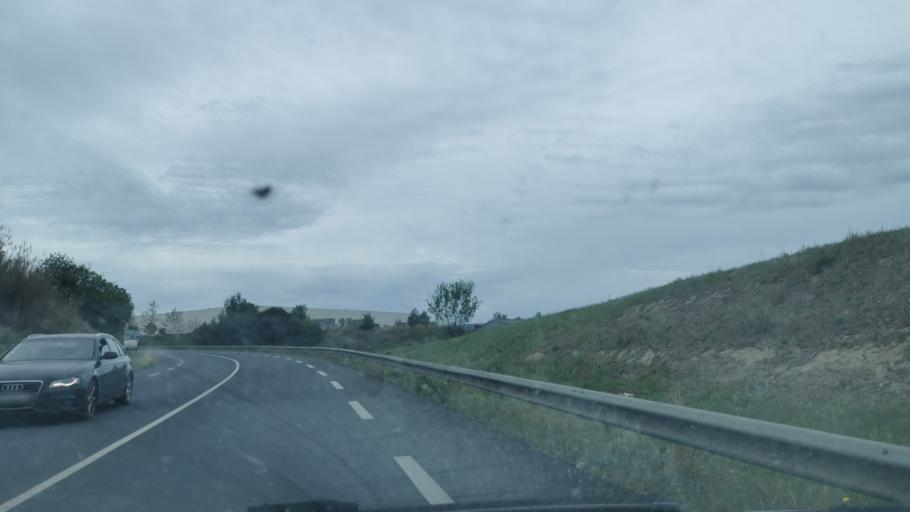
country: FR
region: Languedoc-Roussillon
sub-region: Departement de l'Herault
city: Gigean
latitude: 43.4915
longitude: 3.7013
